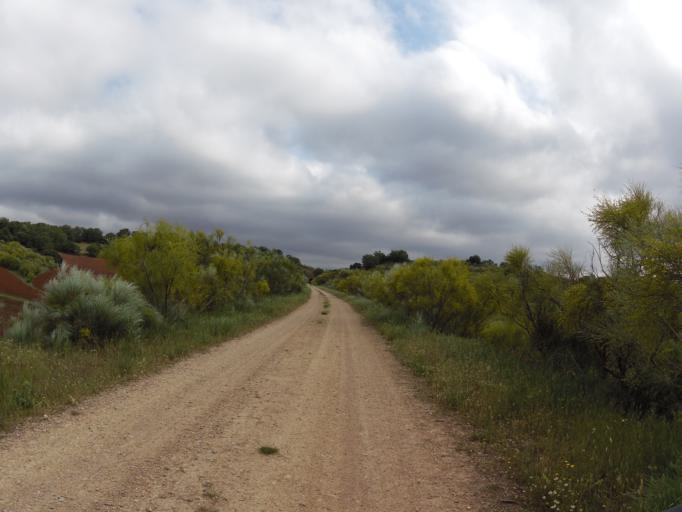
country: ES
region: Castille-La Mancha
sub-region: Provincia de Albacete
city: Robledo
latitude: 38.7233
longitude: -2.4792
